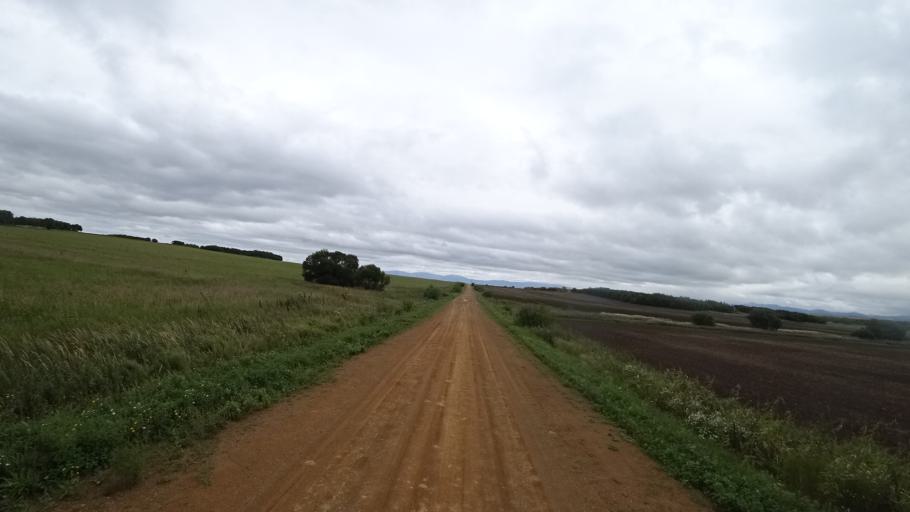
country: RU
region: Primorskiy
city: Chernigovka
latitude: 44.4365
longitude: 132.5844
